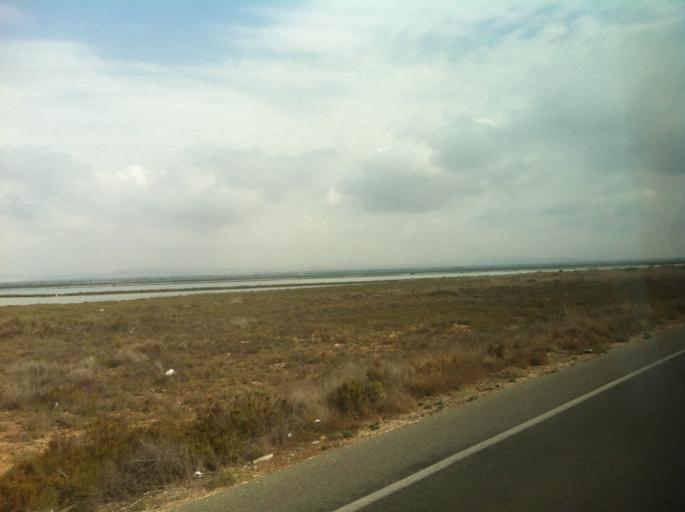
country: ES
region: Valencia
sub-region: Provincia de Alicante
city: Santa Pola
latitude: 38.1678
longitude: -0.6292
